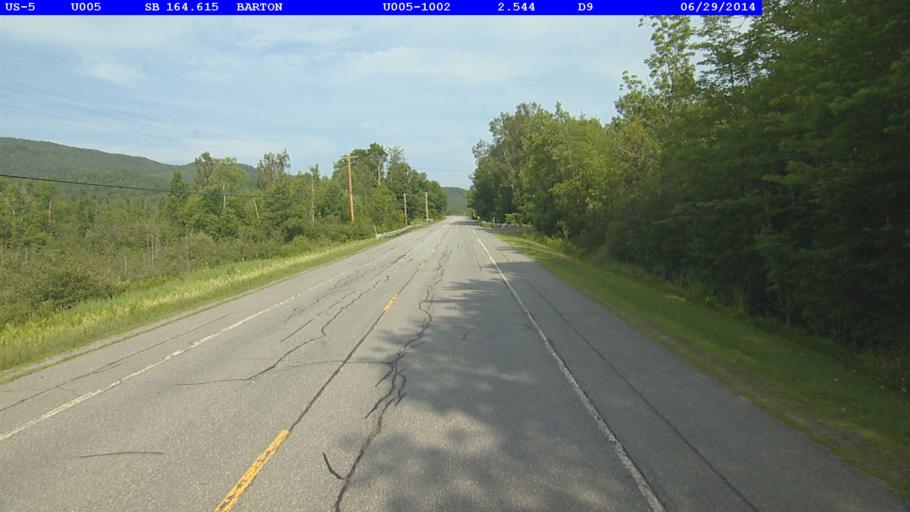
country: US
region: Vermont
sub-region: Caledonia County
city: Lyndonville
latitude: 44.7164
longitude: -72.1404
